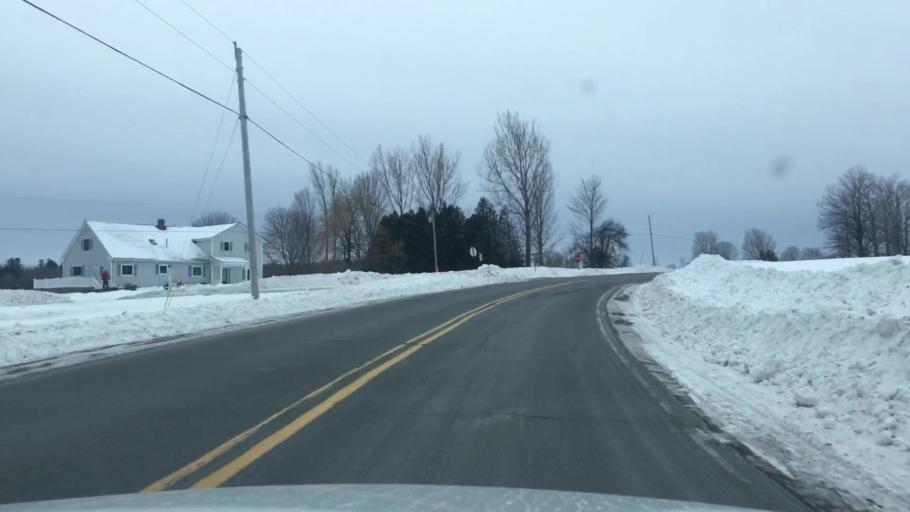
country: US
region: Maine
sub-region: Penobscot County
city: Corinna
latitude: 44.9470
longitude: -69.2055
